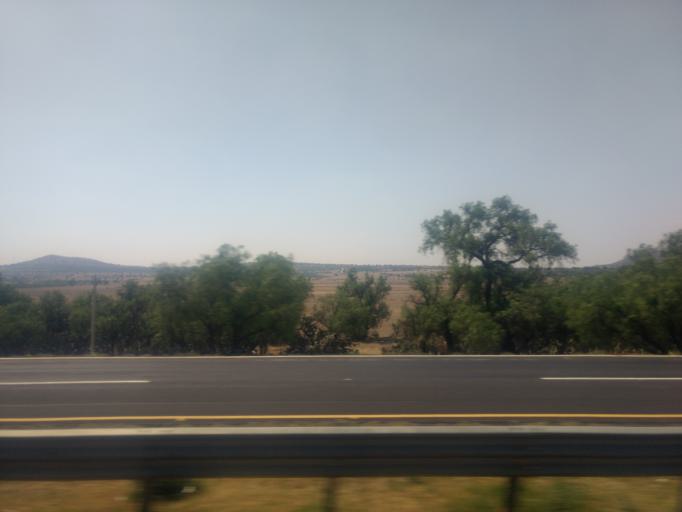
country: MX
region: Morelos
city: Nopaltepec
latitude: 19.8053
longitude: -98.7227
